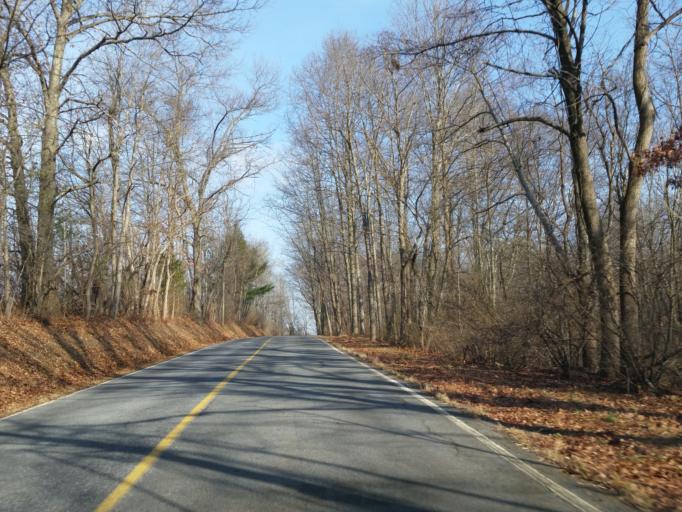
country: US
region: Pennsylvania
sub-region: Schuylkill County
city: Tower City
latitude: 40.4918
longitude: -76.5498
